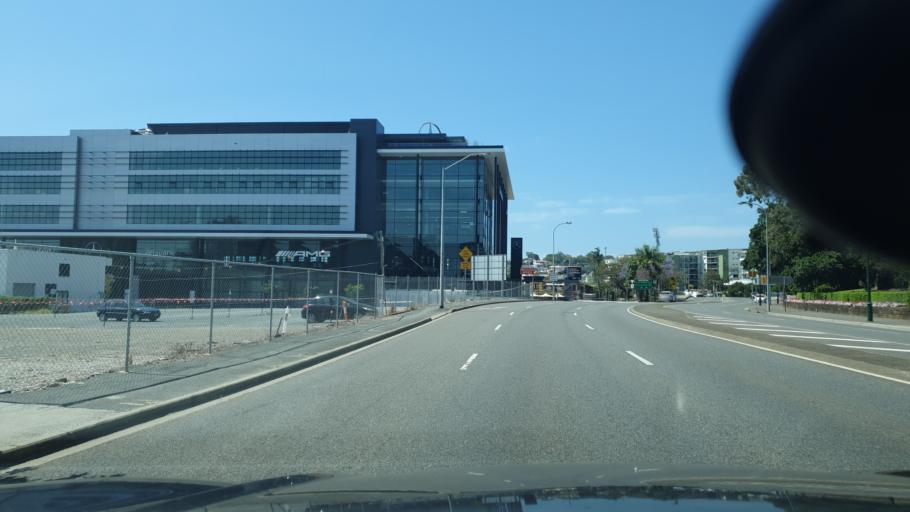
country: AU
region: Queensland
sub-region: Brisbane
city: Windsor
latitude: -27.4429
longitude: 153.0441
